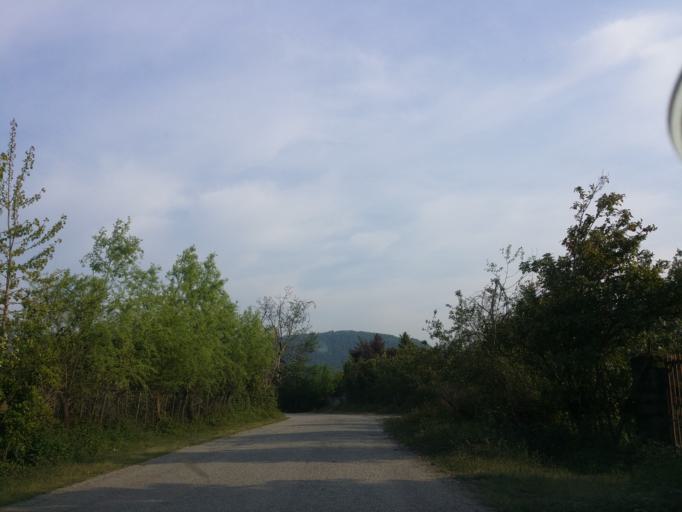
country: IR
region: Mazandaran
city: Chalus
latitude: 36.6624
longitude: 51.3650
